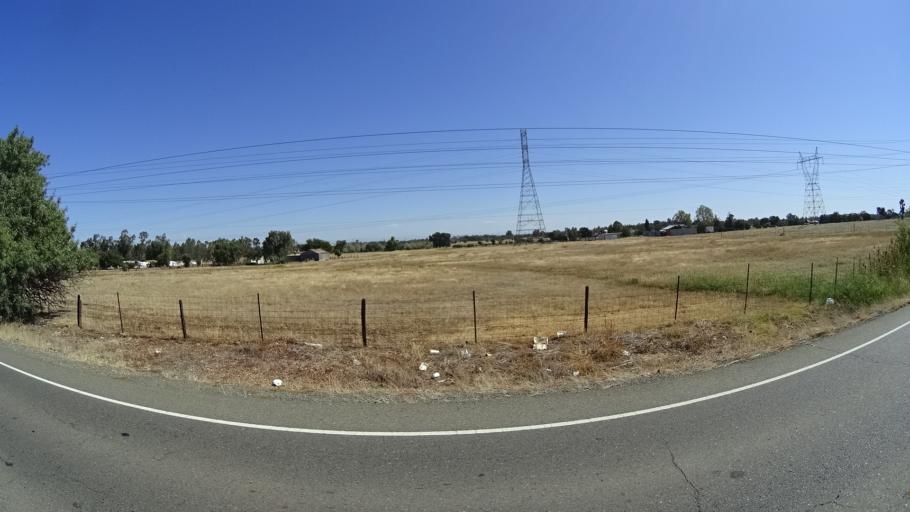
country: US
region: California
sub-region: Sacramento County
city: Vineyard
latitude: 38.4442
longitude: -121.3533
